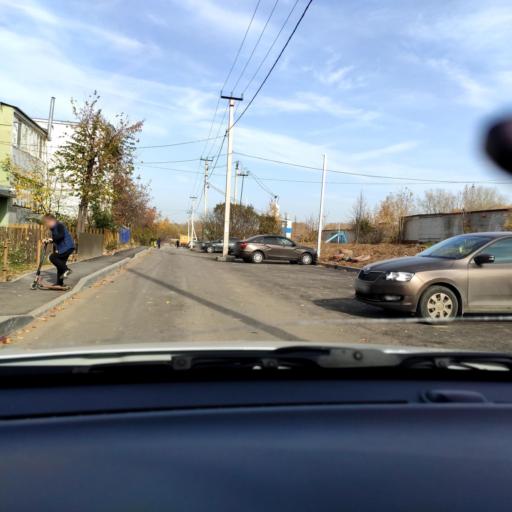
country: RU
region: Tatarstan
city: Vysokaya Gora
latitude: 55.8074
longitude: 49.2716
